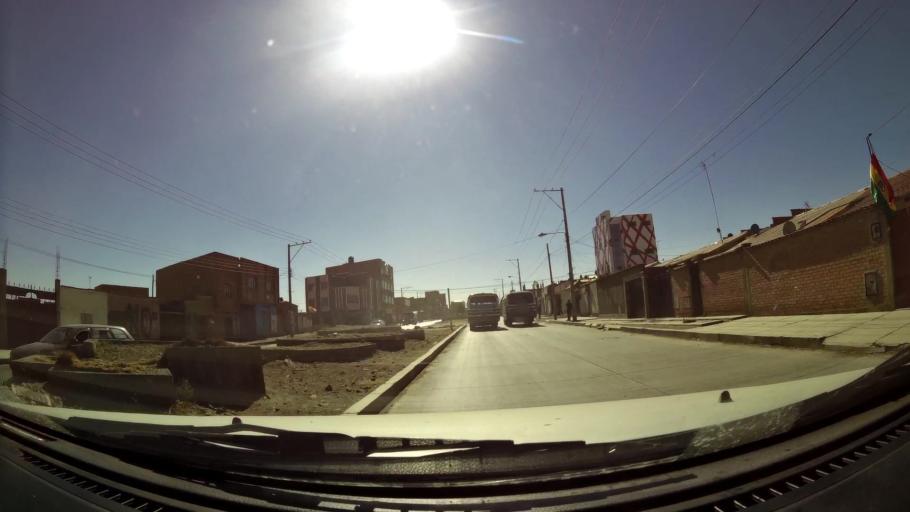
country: BO
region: La Paz
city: La Paz
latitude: -16.5335
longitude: -68.2156
